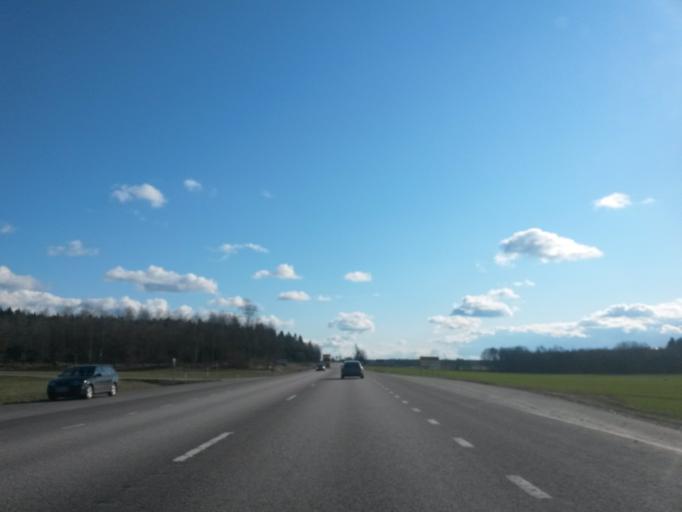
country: SE
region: Vaestra Goetaland
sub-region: Vargarda Kommun
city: Vargarda
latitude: 58.1153
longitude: 12.8442
